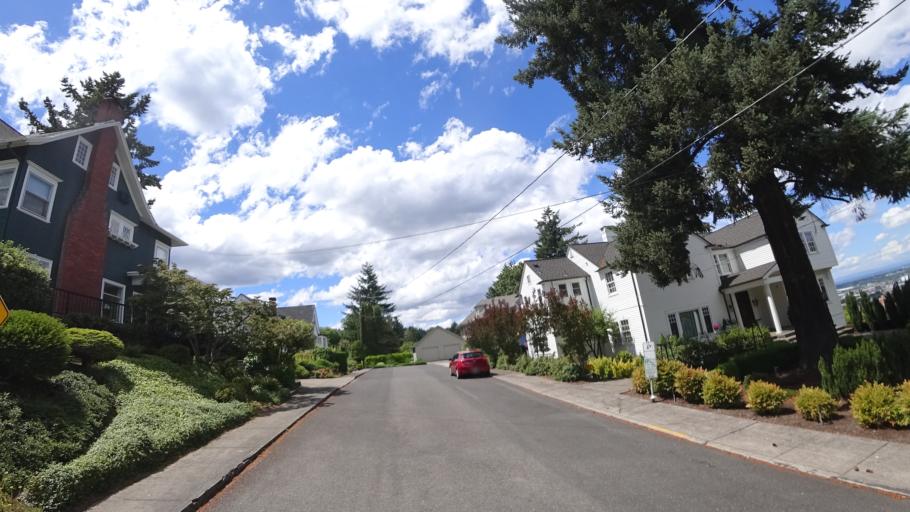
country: US
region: Oregon
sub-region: Multnomah County
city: Portland
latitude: 45.5123
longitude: -122.6933
